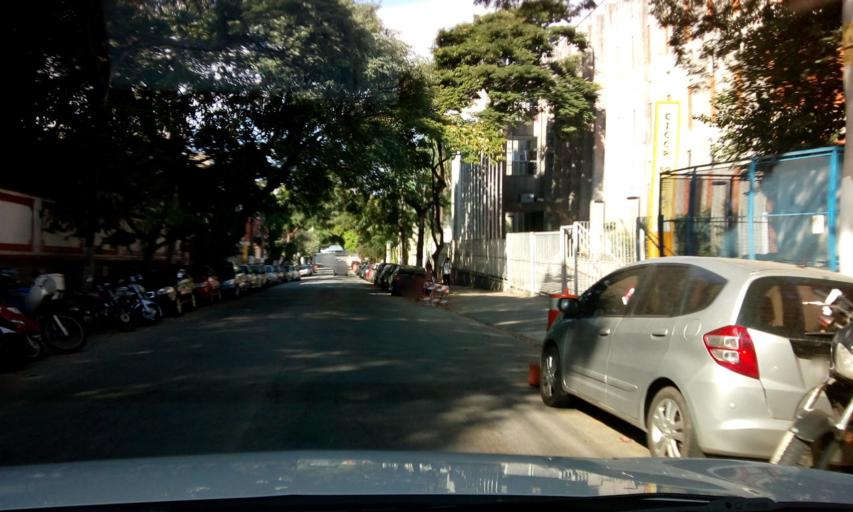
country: BR
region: Sao Paulo
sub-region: Sao Paulo
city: Sao Paulo
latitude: -23.5321
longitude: -46.6281
